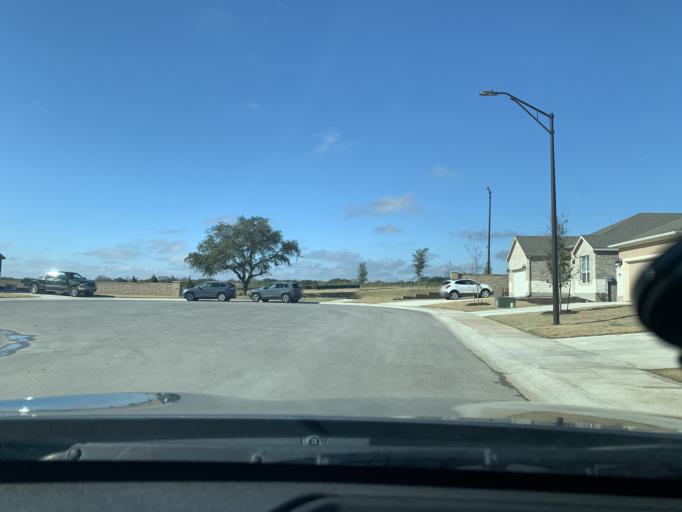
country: US
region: Texas
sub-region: Williamson County
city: Serenada
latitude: 30.7307
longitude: -97.7593
